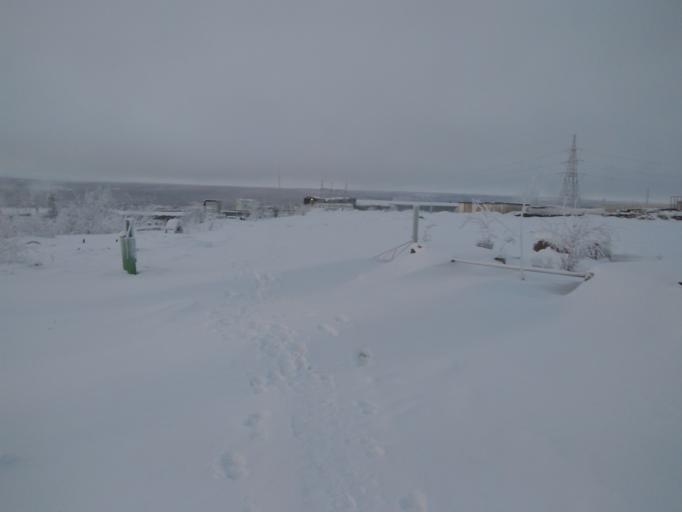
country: RU
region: Sakha
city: Aykhal
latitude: 65.9354
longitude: 111.5095
